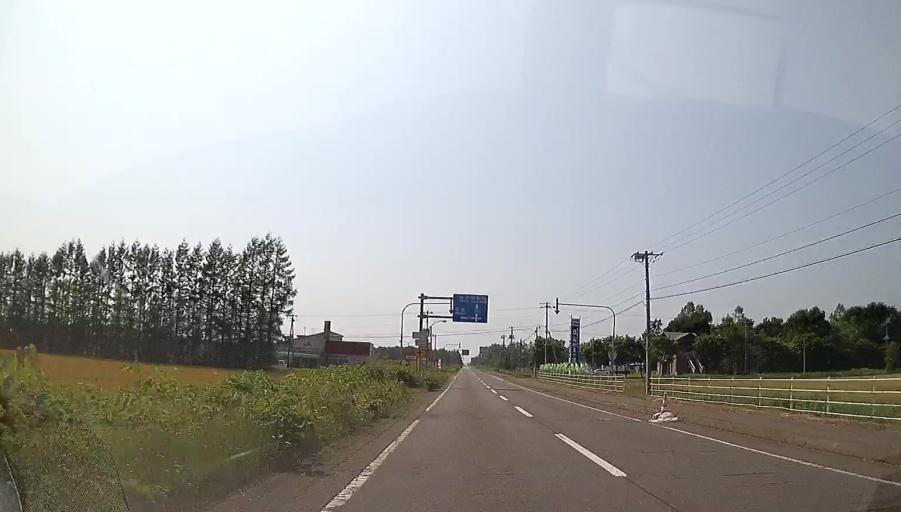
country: JP
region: Hokkaido
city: Otofuke
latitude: 43.1701
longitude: 143.1120
